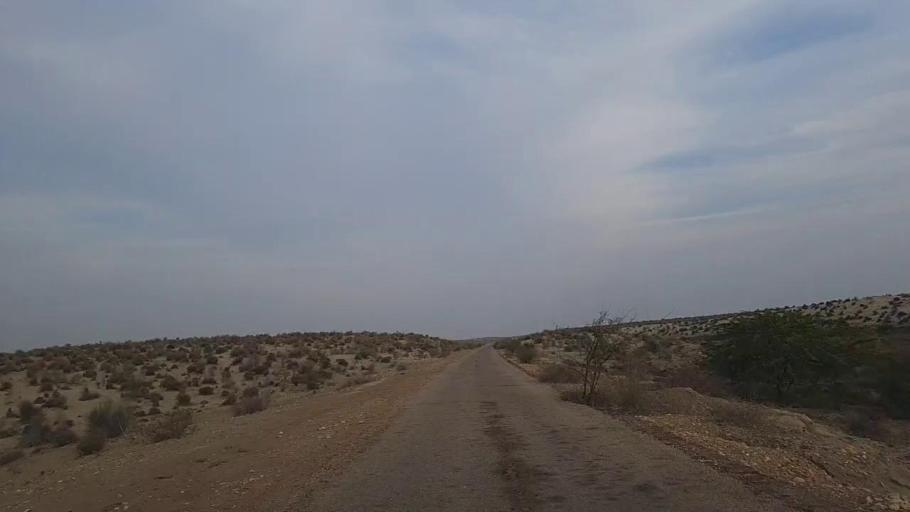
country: PK
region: Sindh
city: Jam Sahib
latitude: 26.4938
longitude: 68.5369
